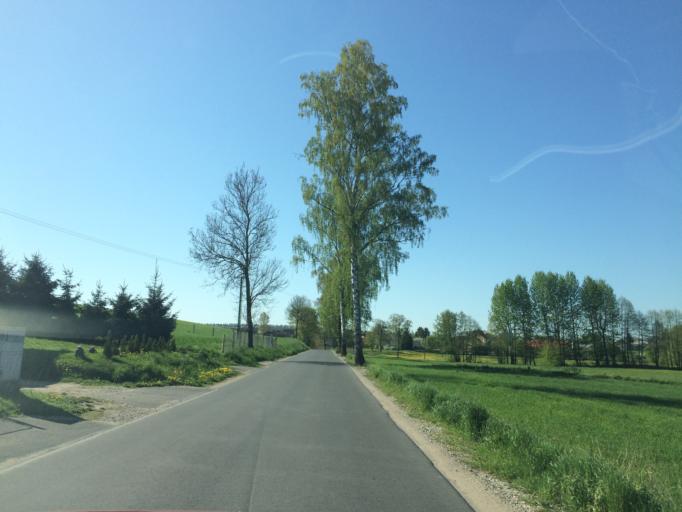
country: PL
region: Warmian-Masurian Voivodeship
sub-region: Powiat nowomiejski
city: Nowe Miasto Lubawskie
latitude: 53.4845
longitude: 19.5741
